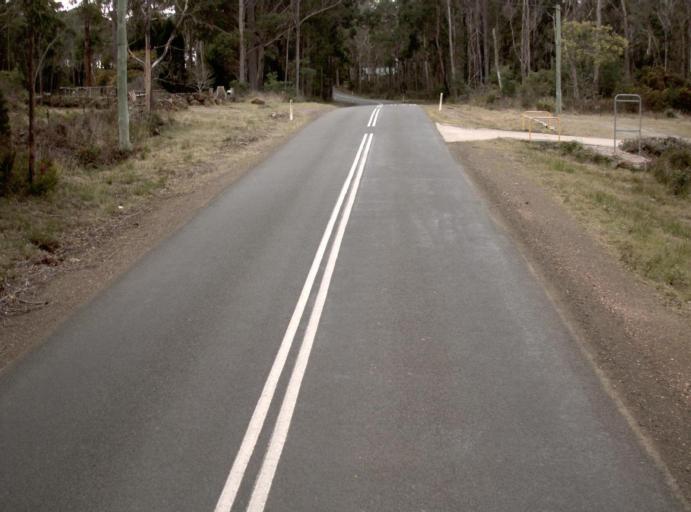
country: AU
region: Tasmania
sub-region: Launceston
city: Mayfield
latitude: -41.2803
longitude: 147.1265
